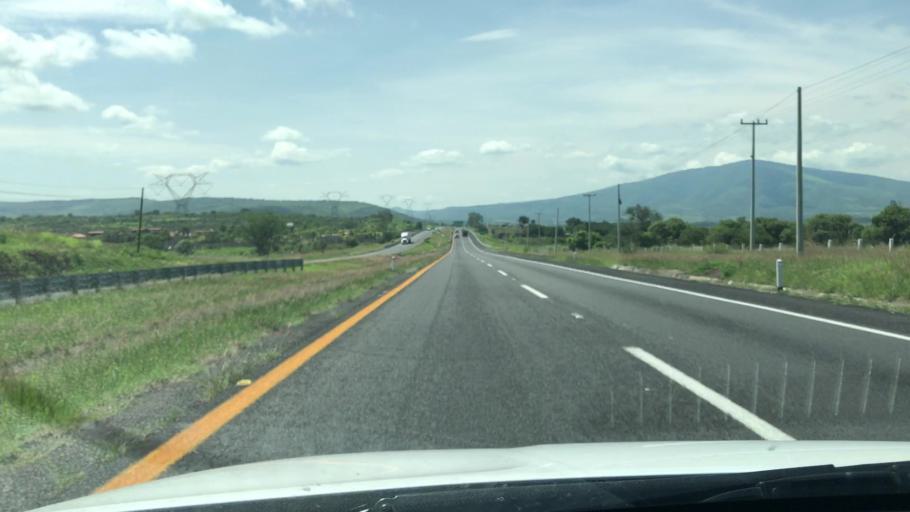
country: MX
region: Jalisco
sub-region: Zapotlanejo
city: La Mezquitera
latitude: 20.5964
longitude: -103.1125
